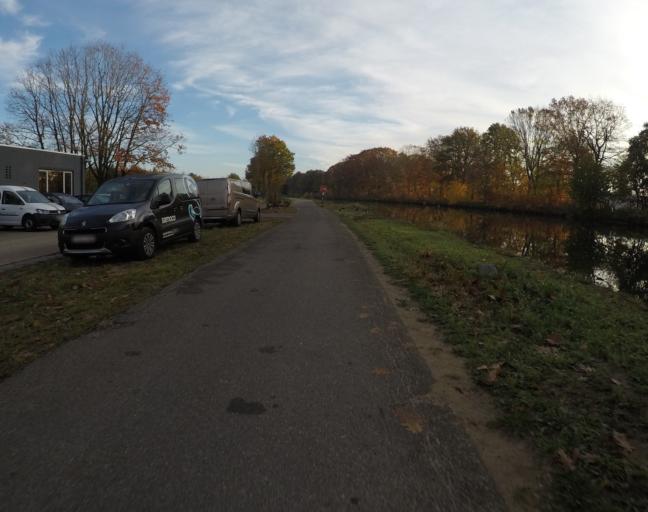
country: BE
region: Flanders
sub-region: Provincie Antwerpen
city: Herentals
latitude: 51.1714
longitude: 4.8495
